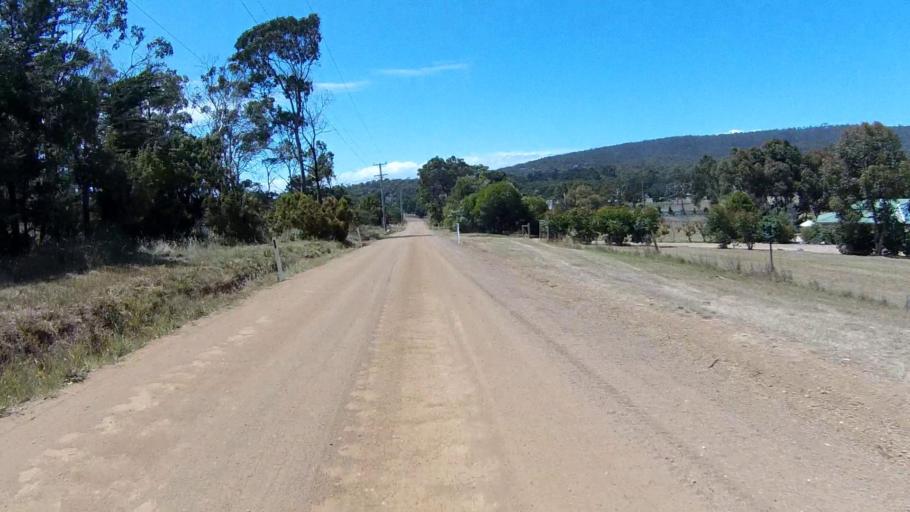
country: AU
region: Tasmania
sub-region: Clarence
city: Sandford
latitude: -42.9663
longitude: 147.4700
